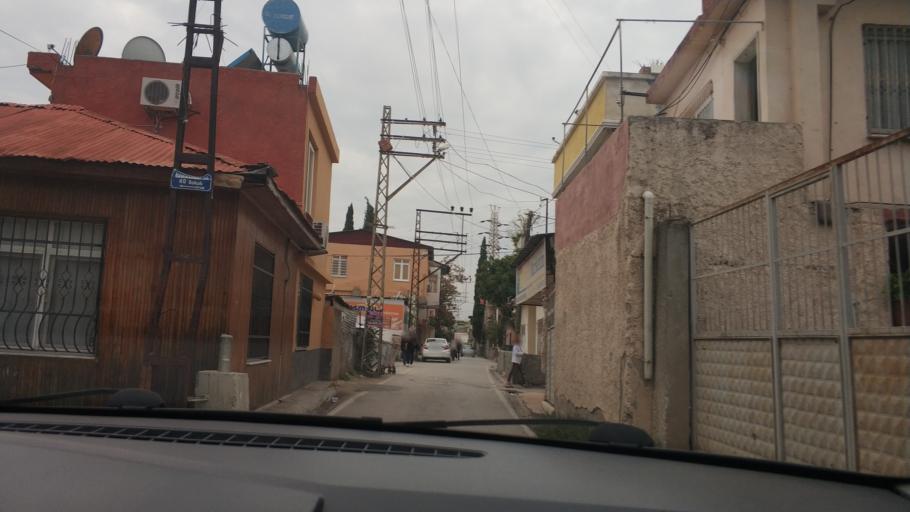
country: TR
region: Adana
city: Adana
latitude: 37.0088
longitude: 35.3144
